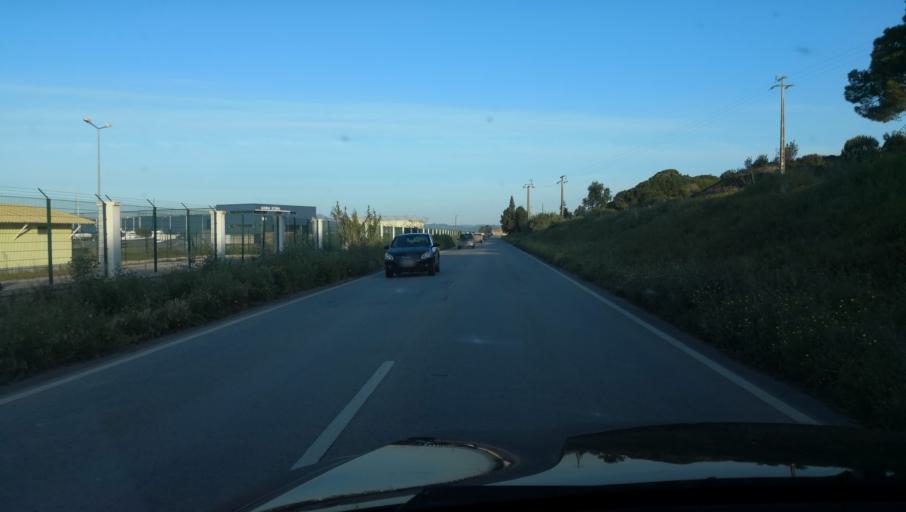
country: PT
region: Setubal
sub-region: Setubal
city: Setubal
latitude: 38.4921
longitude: -8.8222
